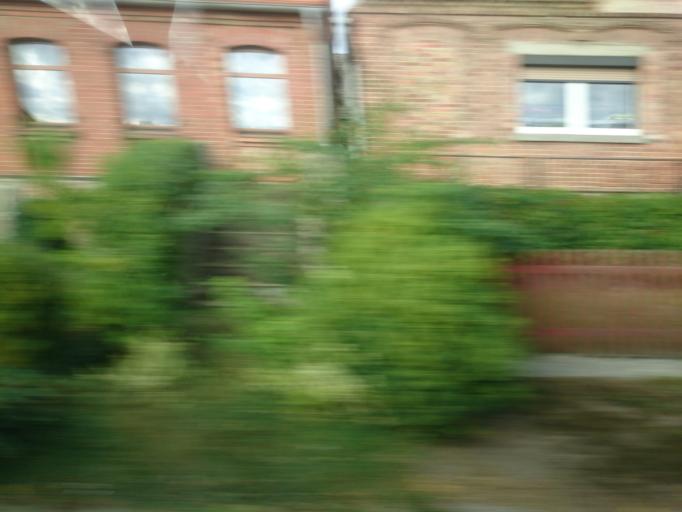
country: DE
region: Mecklenburg-Vorpommern
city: Pasewalk
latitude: 53.5448
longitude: 13.9694
